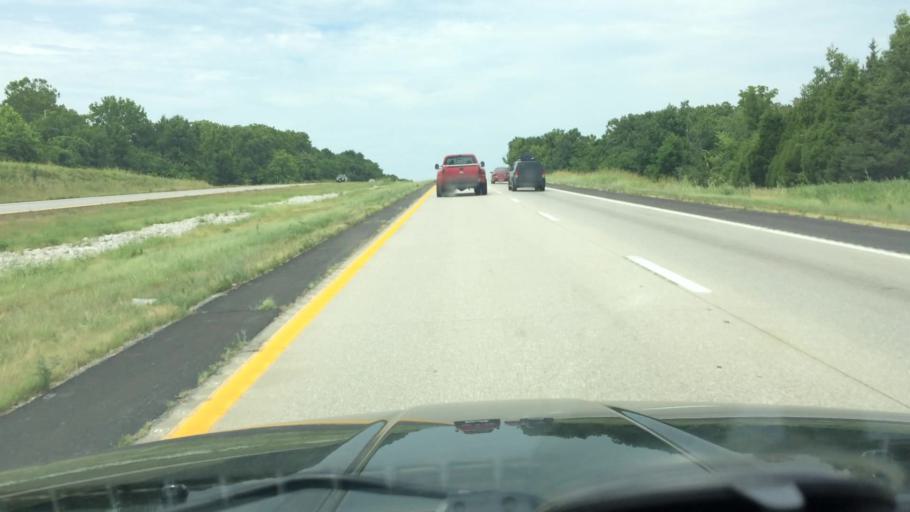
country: US
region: Missouri
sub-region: Greene County
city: Willard
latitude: 37.4416
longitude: -93.3554
